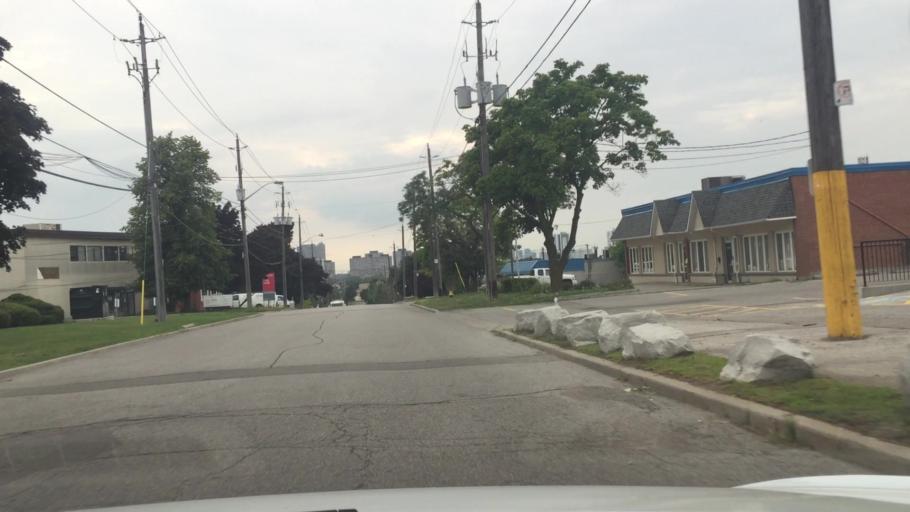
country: CA
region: Ontario
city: Scarborough
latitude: 43.7165
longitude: -79.3066
